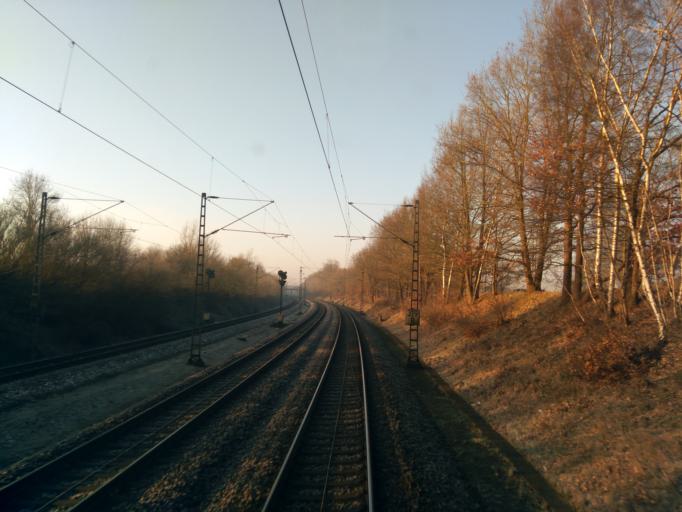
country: DE
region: Lower Saxony
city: Buchholz in der Nordheide
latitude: 53.3178
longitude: 9.8274
